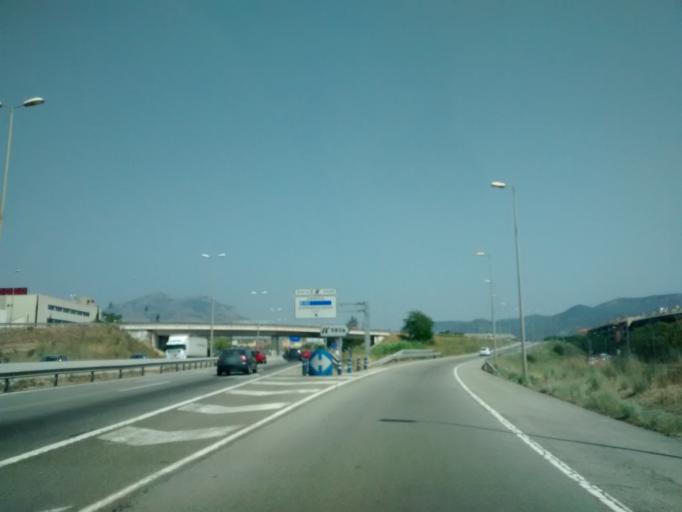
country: ES
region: Catalonia
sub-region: Provincia de Barcelona
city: Abrera
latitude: 41.5161
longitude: 1.8983
